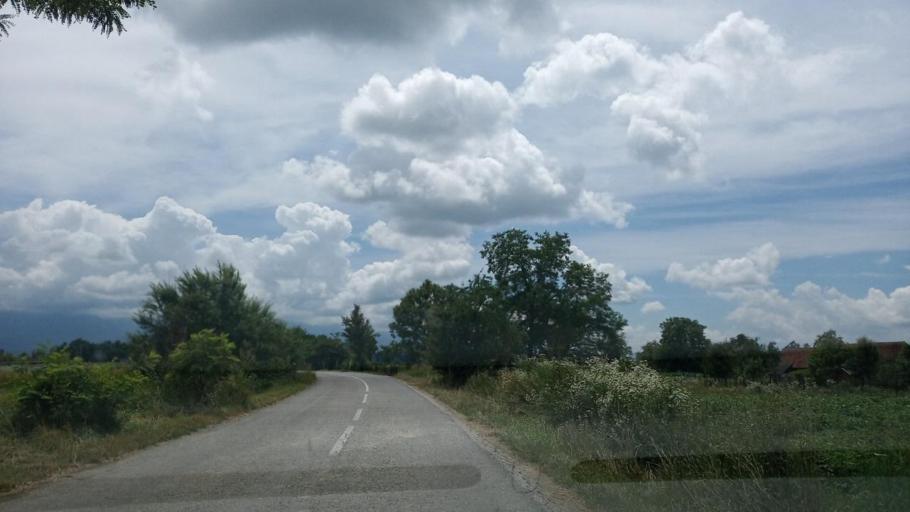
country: RO
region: Sibiu
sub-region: Comuna Porumbacu de Jos
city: Porumbacu de Jos
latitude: 45.7543
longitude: 24.4612
